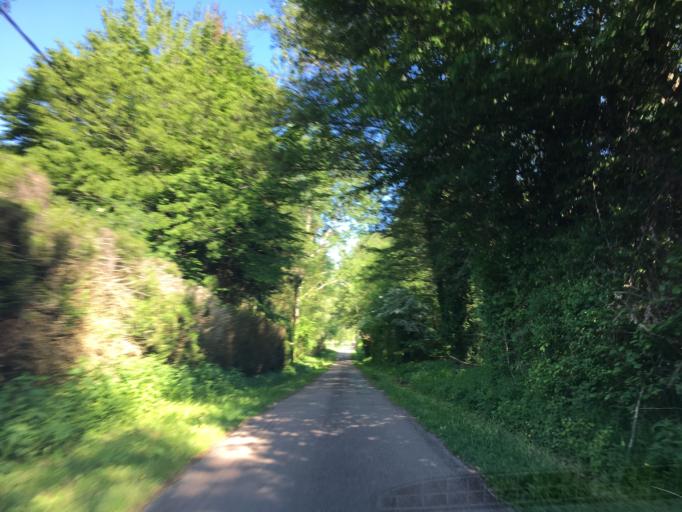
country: FR
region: Bourgogne
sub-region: Departement de l'Yonne
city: Aillant-sur-Tholon
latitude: 47.8220
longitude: 3.3473
